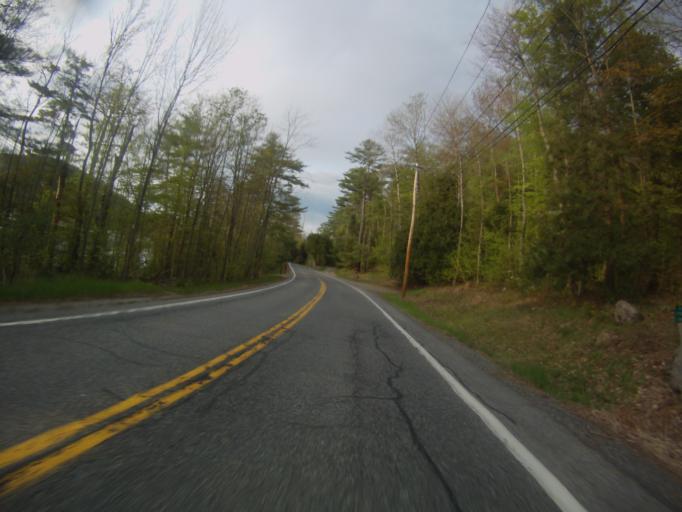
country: US
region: New York
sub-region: Warren County
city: Warrensburg
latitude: 43.7135
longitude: -73.6991
